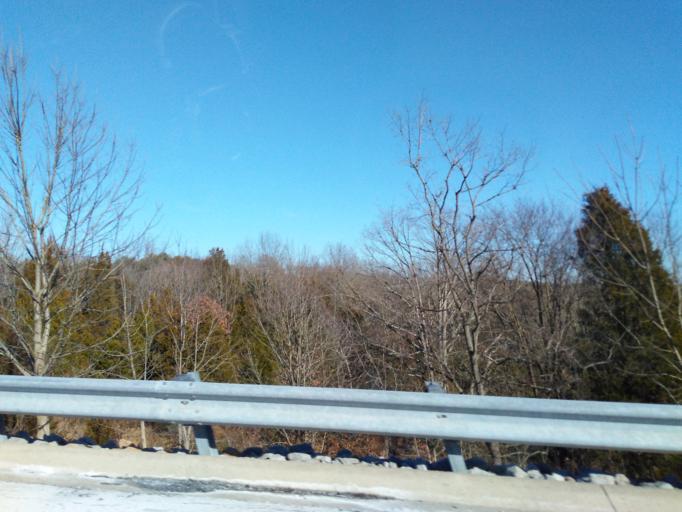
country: US
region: Illinois
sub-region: Johnson County
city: Vienna
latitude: 37.4896
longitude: -88.8933
